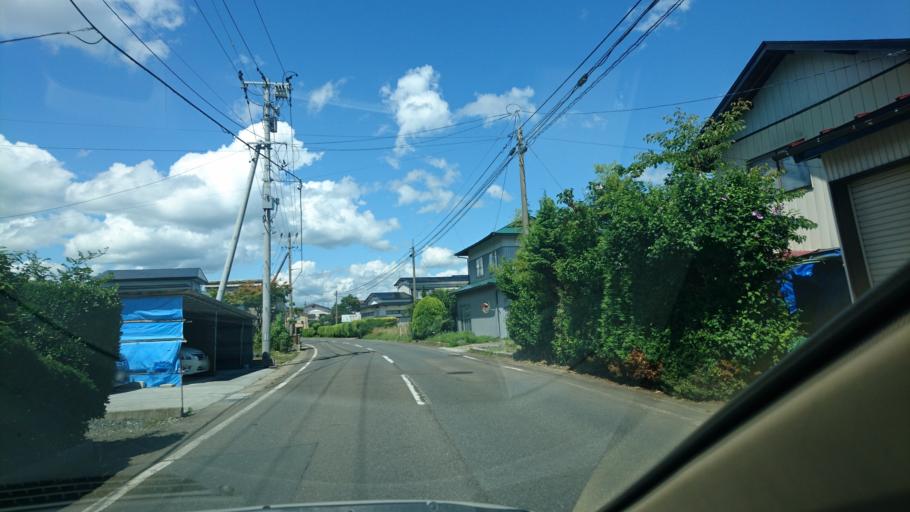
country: JP
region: Iwate
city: Kitakami
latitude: 39.3274
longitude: 141.1416
